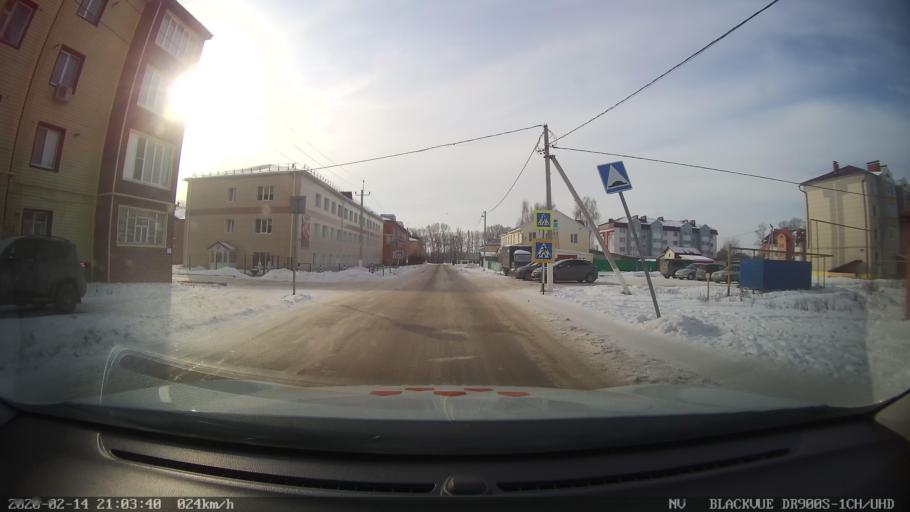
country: RU
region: Tatarstan
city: Kuybyshevskiy Zaton
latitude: 55.1560
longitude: 49.1753
